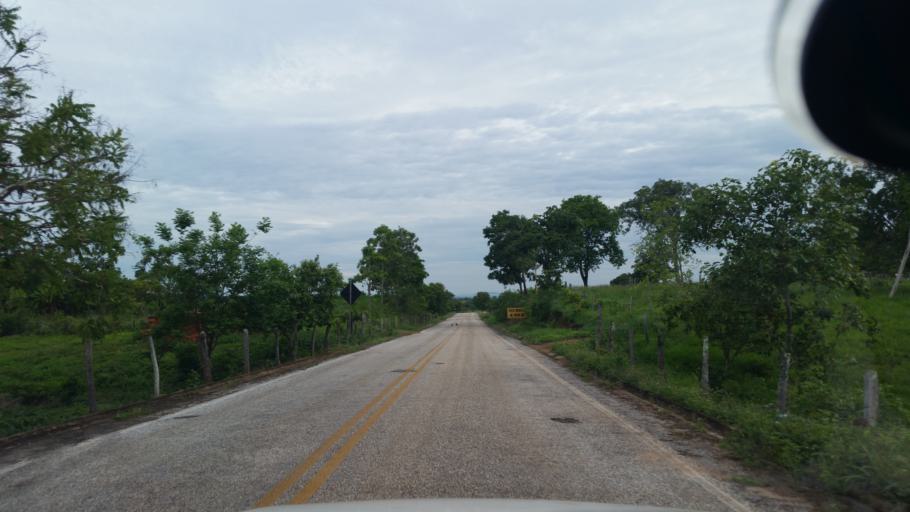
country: BR
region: Goias
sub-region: Uruacu
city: Uruacu
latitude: -14.0170
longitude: -49.1682
